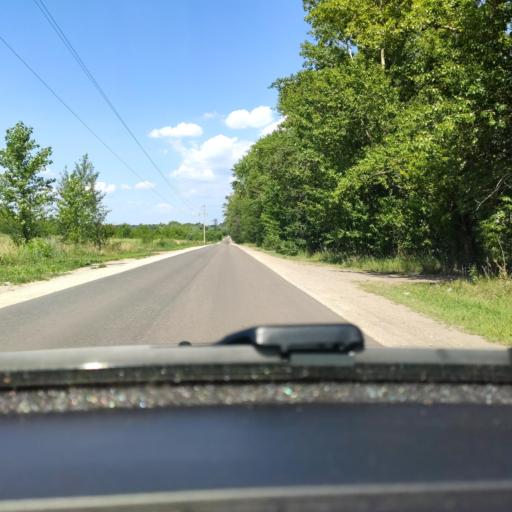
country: RU
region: Voronezj
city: Maslovka
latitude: 51.5124
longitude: 39.2200
